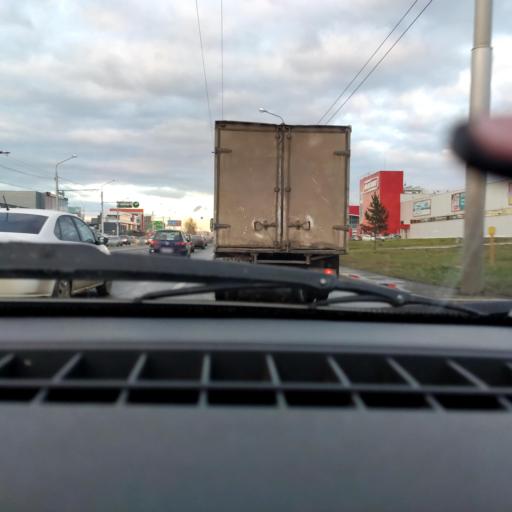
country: RU
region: Bashkortostan
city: Ufa
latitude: 54.7815
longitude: 56.0727
